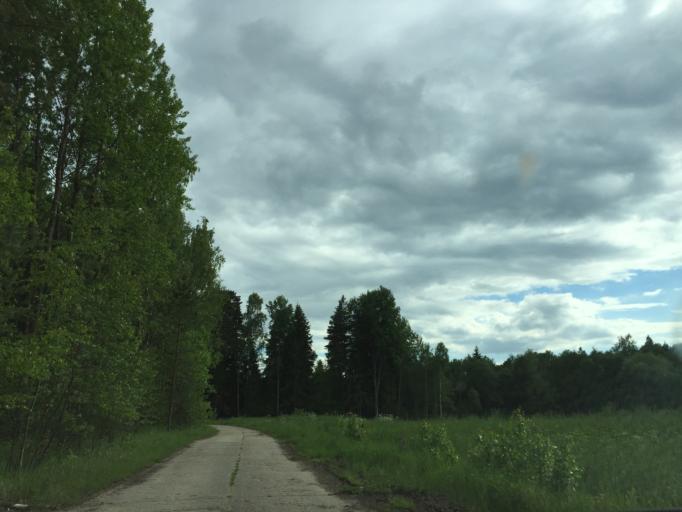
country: LV
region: Dobeles Rajons
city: Dobele
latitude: 56.6410
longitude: 23.1749
